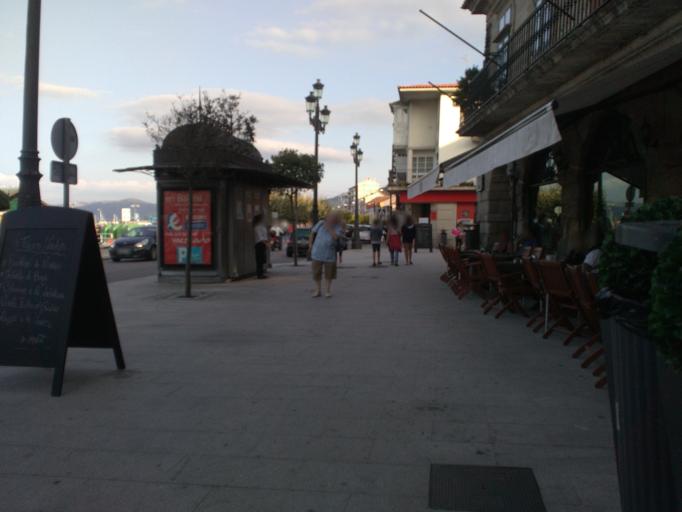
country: ES
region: Galicia
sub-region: Provincia de Pontevedra
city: Baiona
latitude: 42.1194
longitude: -8.8482
